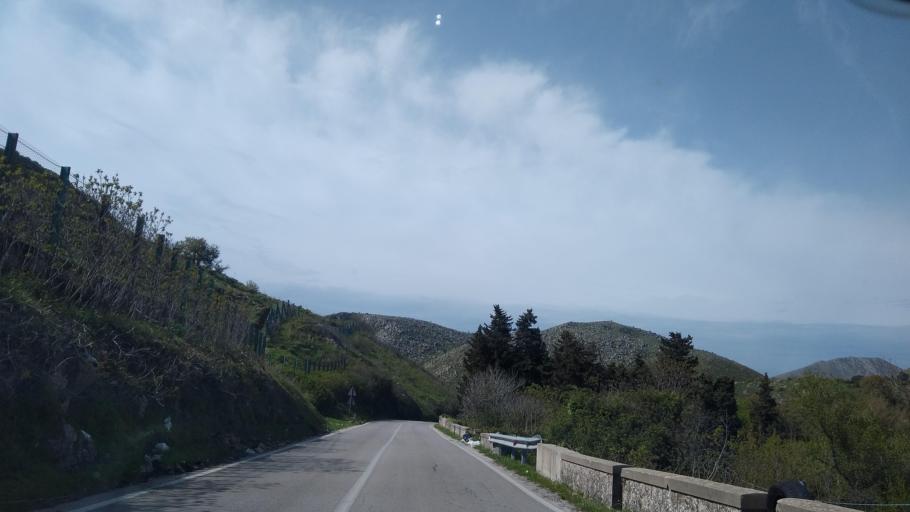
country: IT
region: Sicily
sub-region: Palermo
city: Pioppo
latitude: 38.0434
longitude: 13.1995
